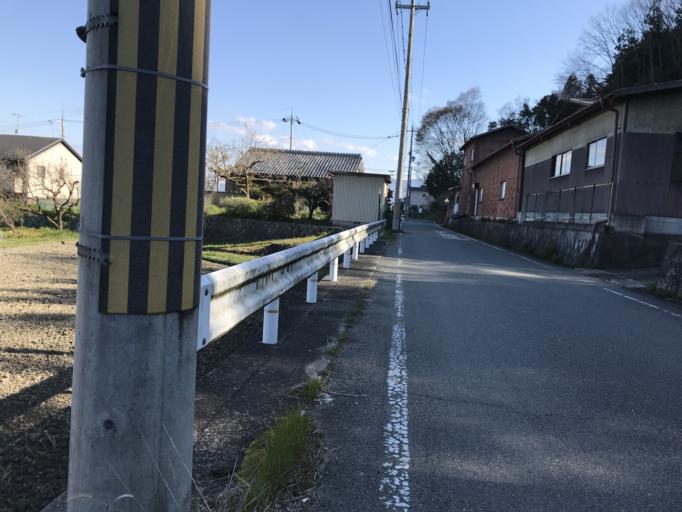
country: JP
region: Kyoto
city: Kameoka
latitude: 35.0028
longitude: 135.5578
